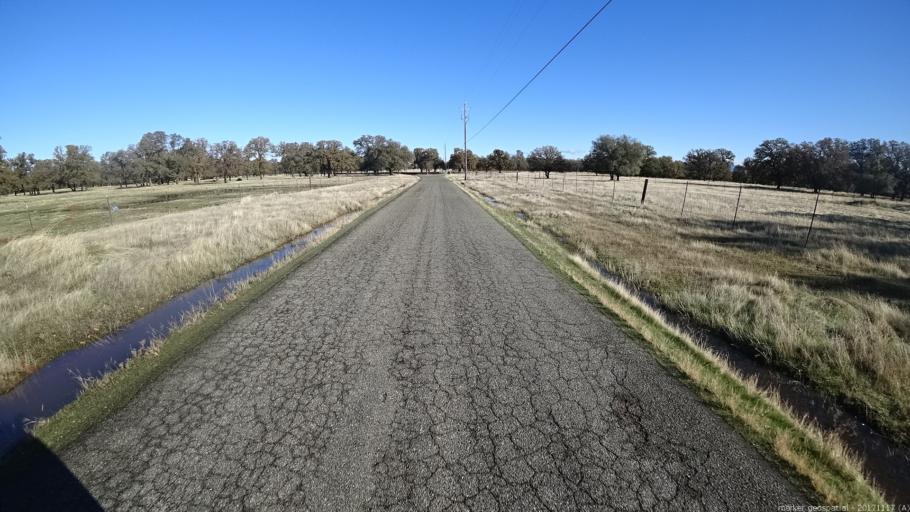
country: US
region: California
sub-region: Shasta County
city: Anderson
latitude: 40.4623
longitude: -122.1918
